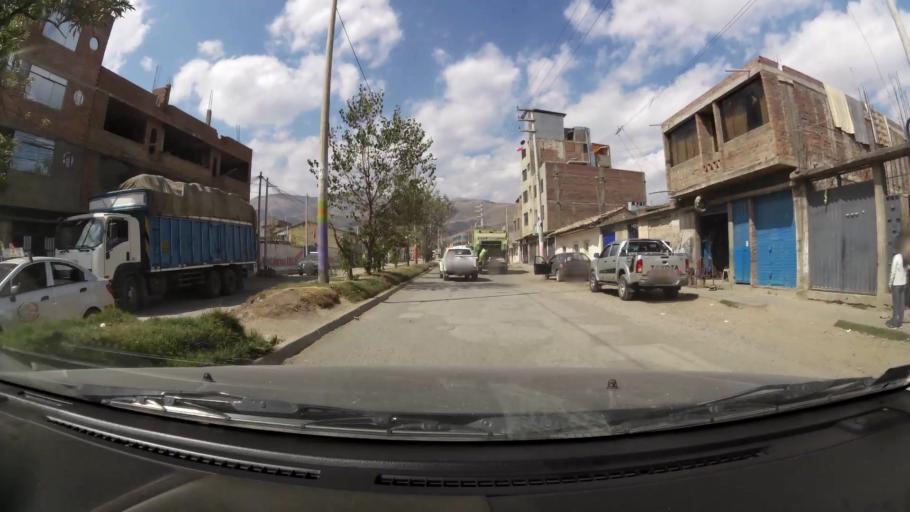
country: PE
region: Junin
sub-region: Provincia de Huancayo
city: Huancayo
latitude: -12.0899
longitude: -75.2075
